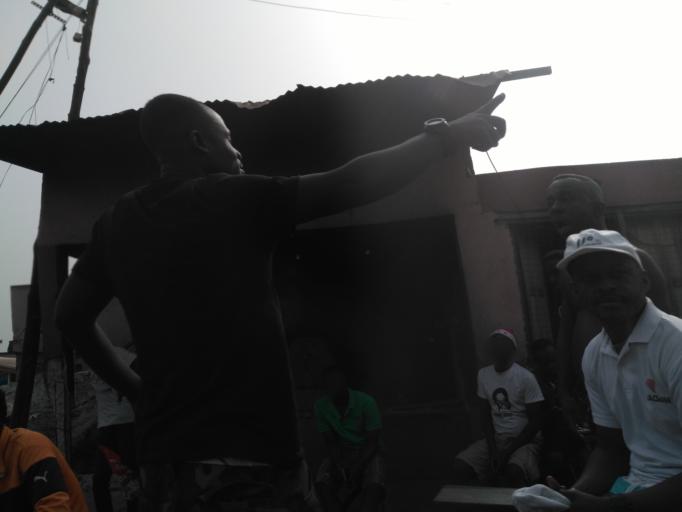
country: GH
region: Ashanti
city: Kumasi
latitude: 6.7015
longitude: -1.6047
